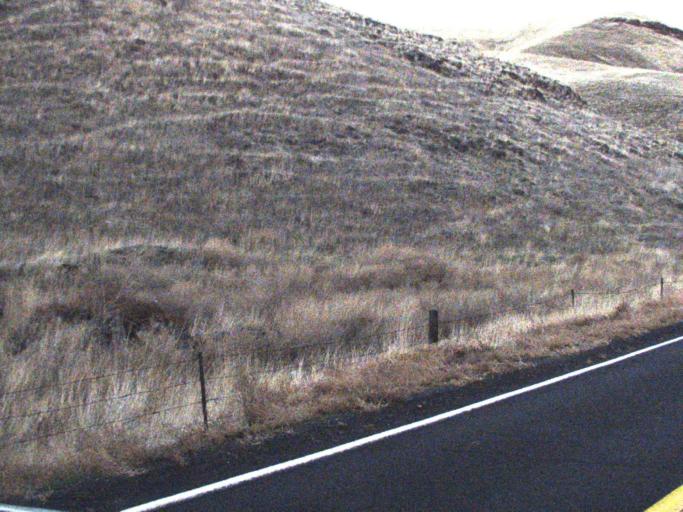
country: US
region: Washington
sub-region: Columbia County
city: Dayton
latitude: 46.5069
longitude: -118.0592
